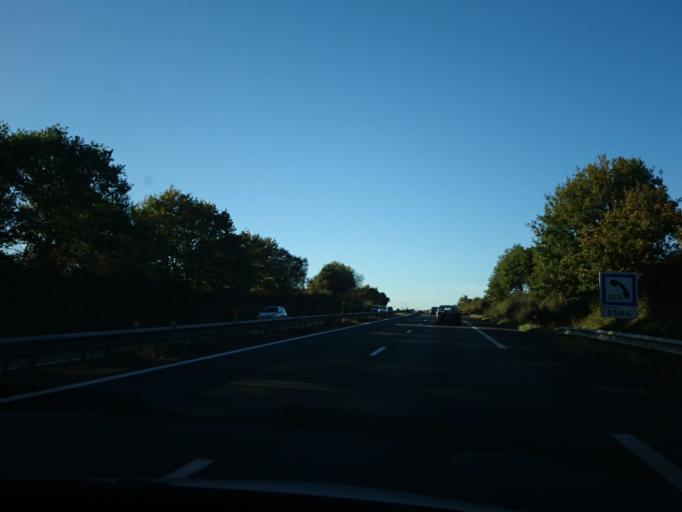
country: FR
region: Brittany
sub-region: Departement des Cotes-d'Armor
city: Caulnes
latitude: 48.2822
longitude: -2.1940
